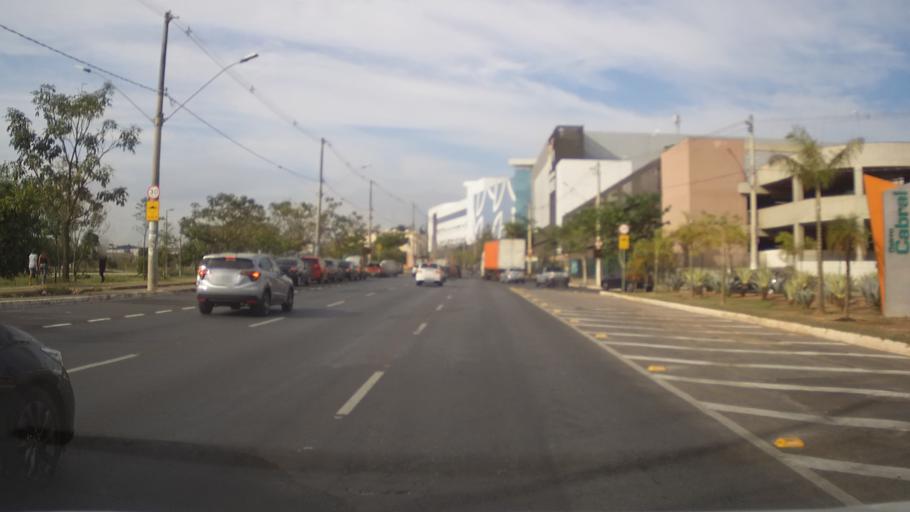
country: BR
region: Minas Gerais
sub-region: Contagem
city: Contagem
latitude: -19.8789
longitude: -44.0363
